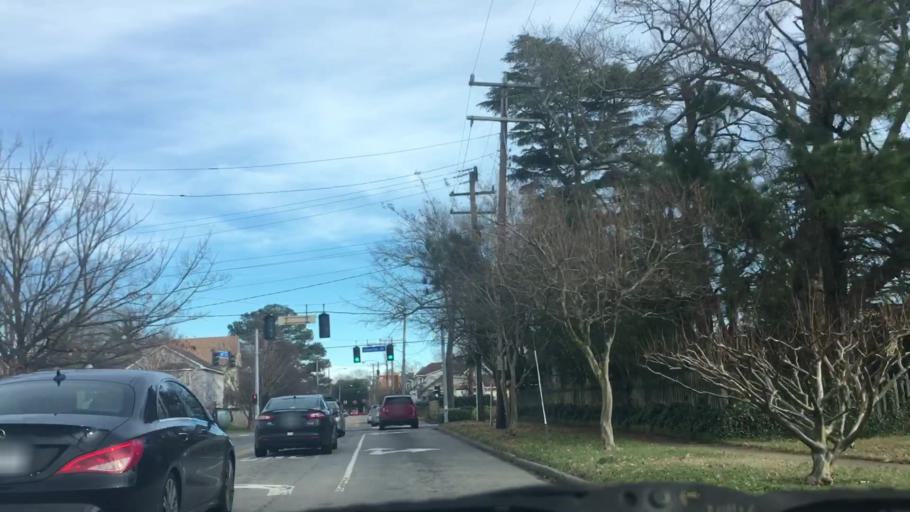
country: US
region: Virginia
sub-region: City of Norfolk
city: Norfolk
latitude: 36.8805
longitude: -76.2857
